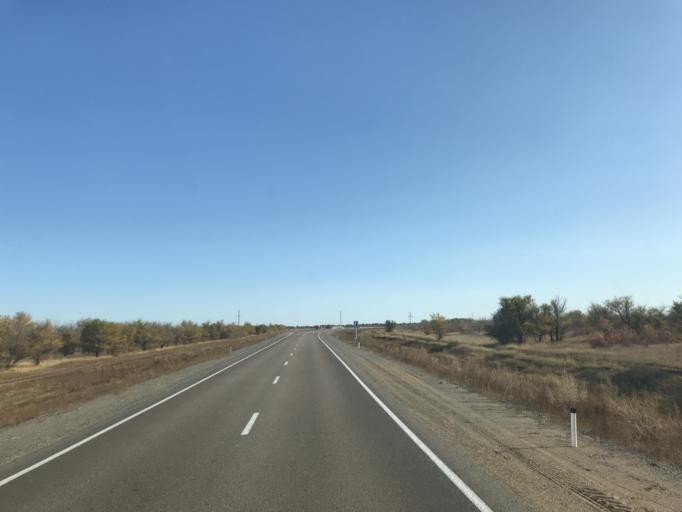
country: KZ
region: Pavlodar
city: Koktobe
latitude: 51.7317
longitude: 77.5557
